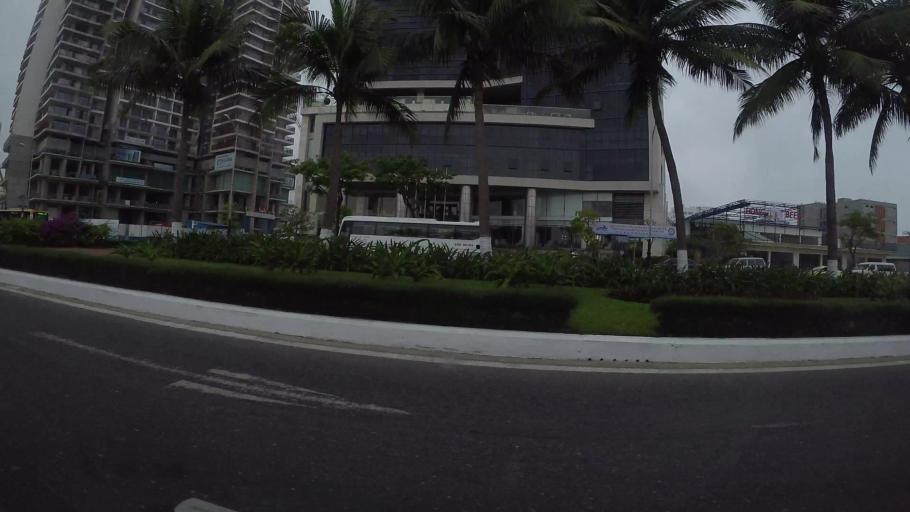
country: VN
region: Da Nang
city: Son Tra
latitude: 16.0721
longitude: 108.2452
